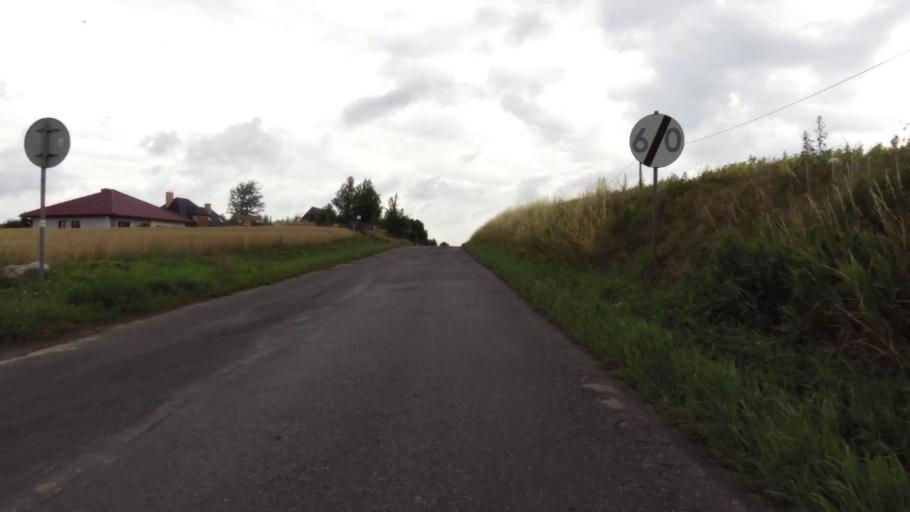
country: PL
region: West Pomeranian Voivodeship
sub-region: Powiat mysliborski
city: Mysliborz
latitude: 52.9420
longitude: 14.8724
